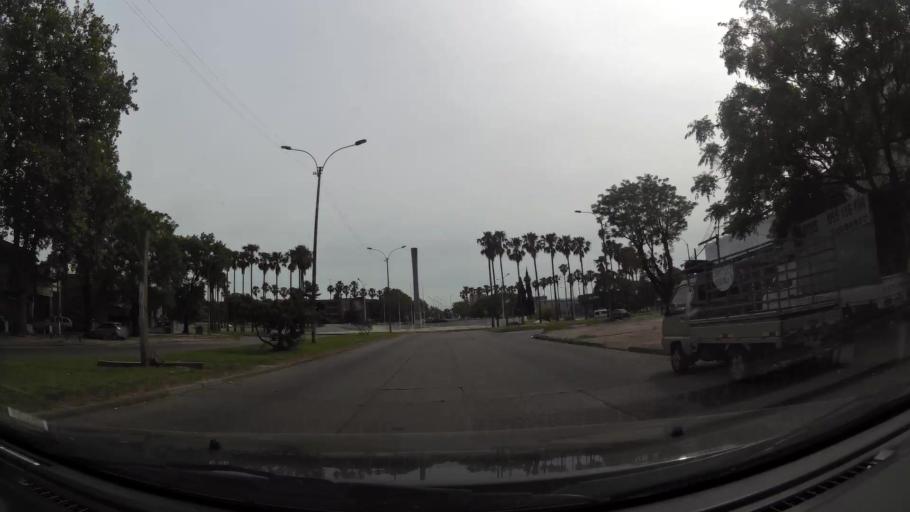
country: UY
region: Montevideo
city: Montevideo
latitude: -34.8643
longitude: -56.1697
